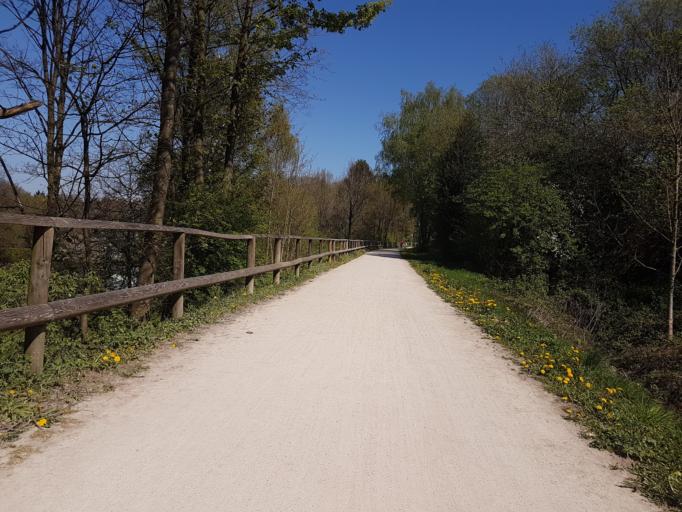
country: DE
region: North Rhine-Westphalia
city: Sprockhovel
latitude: 51.3413
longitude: 7.2871
